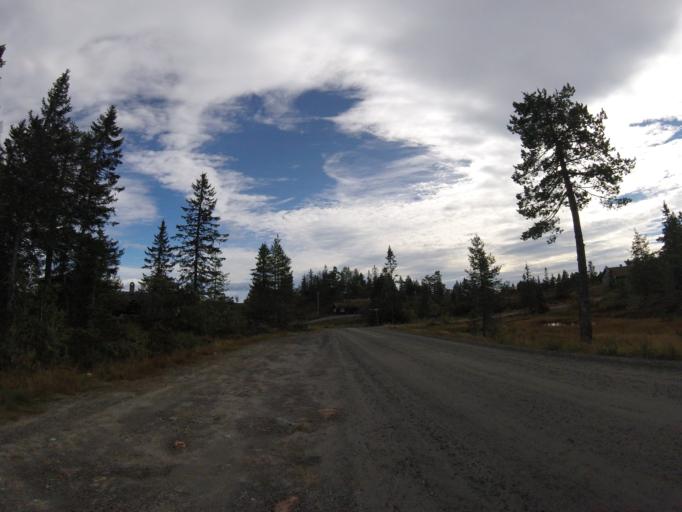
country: NO
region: Buskerud
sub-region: Flesberg
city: Lampeland
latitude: 59.7668
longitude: 9.4613
